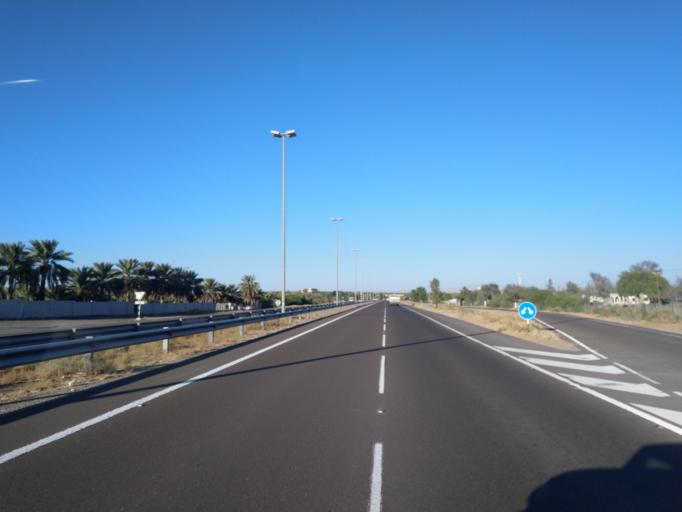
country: OM
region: Al Buraimi
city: Al Buraymi
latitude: 24.5568
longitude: 55.6915
